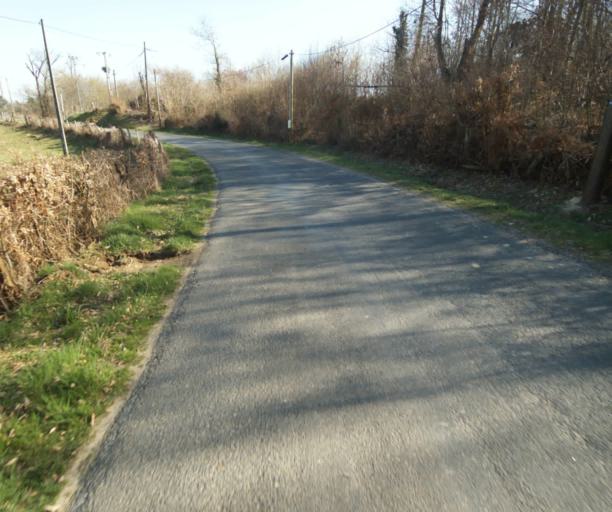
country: FR
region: Limousin
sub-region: Departement de la Correze
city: Saint-Mexant
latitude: 45.3127
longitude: 1.6136
